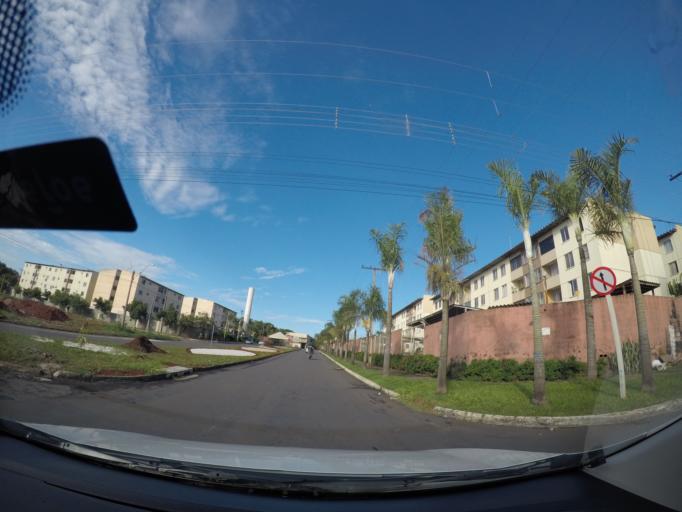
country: BR
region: Goias
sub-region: Goiania
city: Goiania
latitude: -16.7487
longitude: -49.2736
